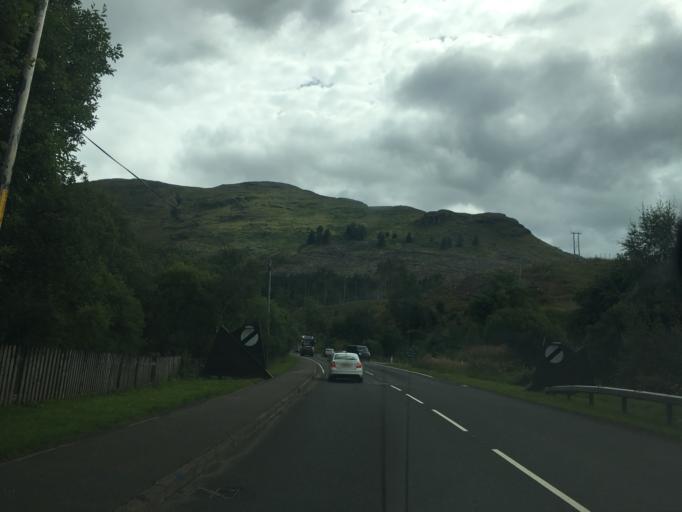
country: GB
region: Scotland
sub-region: Argyll and Bute
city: Garelochhead
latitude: 56.3913
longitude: -4.6112
